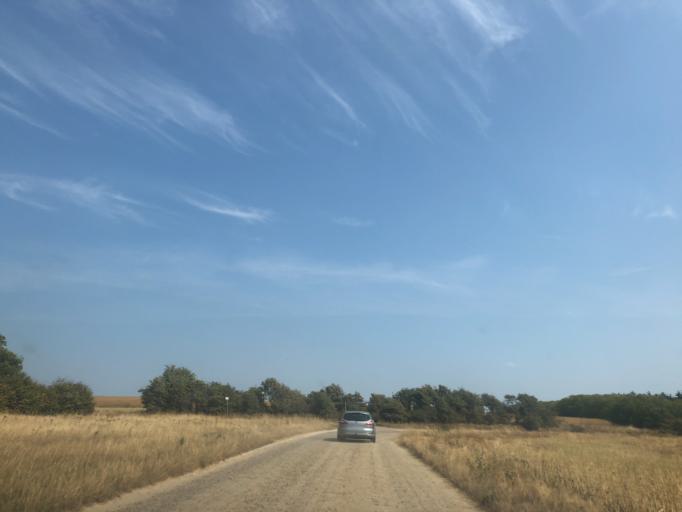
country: DK
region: North Denmark
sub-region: Morso Kommune
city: Nykobing Mors
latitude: 56.8246
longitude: 8.9807
